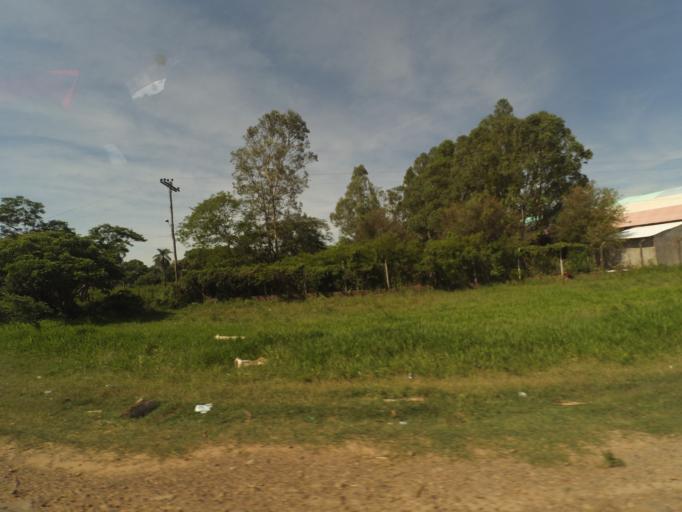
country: BO
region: Santa Cruz
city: Cotoca
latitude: -17.7618
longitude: -63.0114
